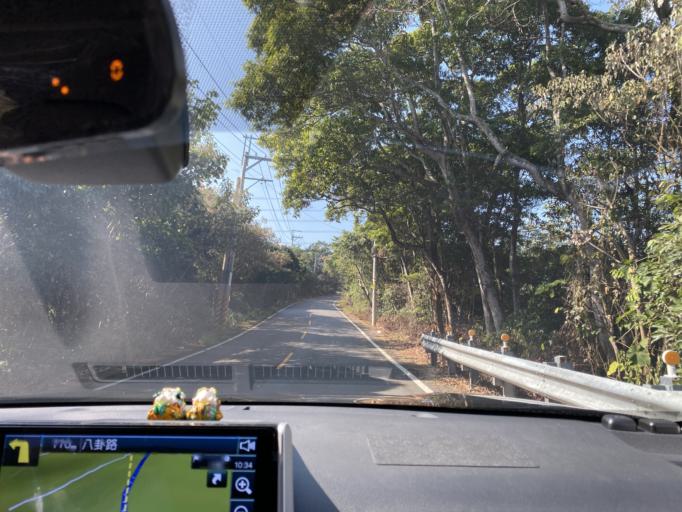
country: TW
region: Taiwan
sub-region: Nantou
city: Nantou
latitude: 23.9373
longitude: 120.6455
